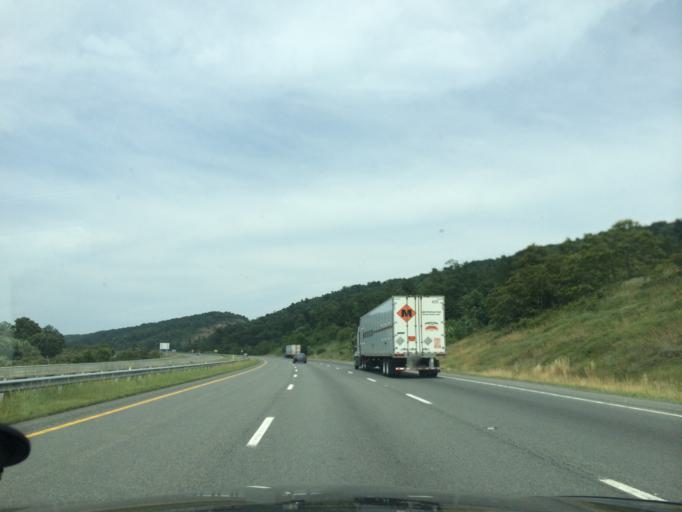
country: US
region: West Virginia
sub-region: Morgan County
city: Berkeley Springs
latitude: 39.7142
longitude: -78.2956
